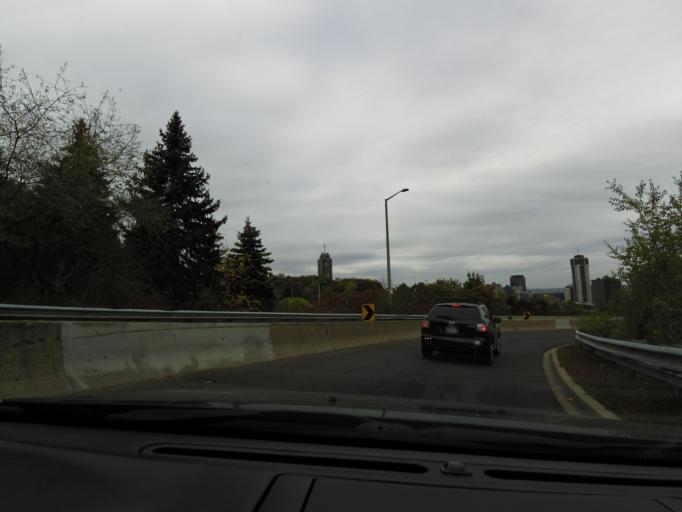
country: CA
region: Ontario
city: Hamilton
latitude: 43.2458
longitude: -79.8609
